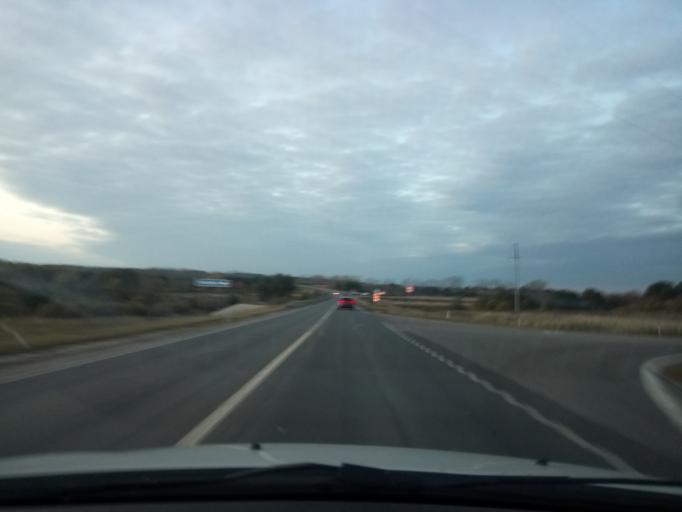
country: RU
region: Nizjnij Novgorod
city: Bol'shoye Murashkino
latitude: 55.8788
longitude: 44.7484
